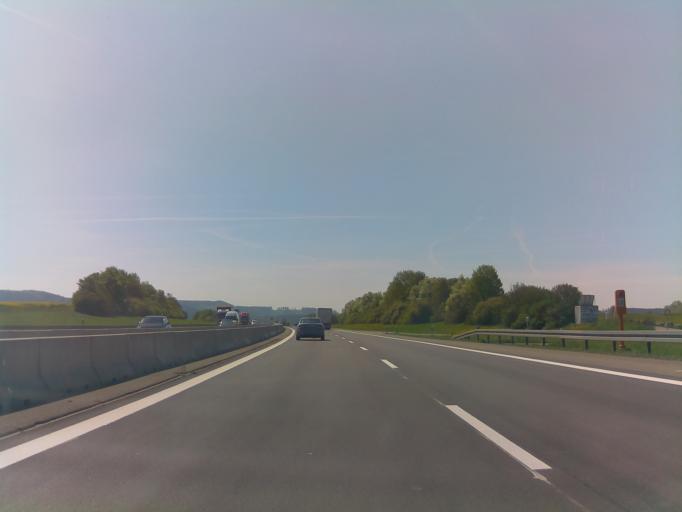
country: DE
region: Baden-Wuerttemberg
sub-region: Freiburg Region
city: Epfendorf
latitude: 48.2650
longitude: 8.6388
